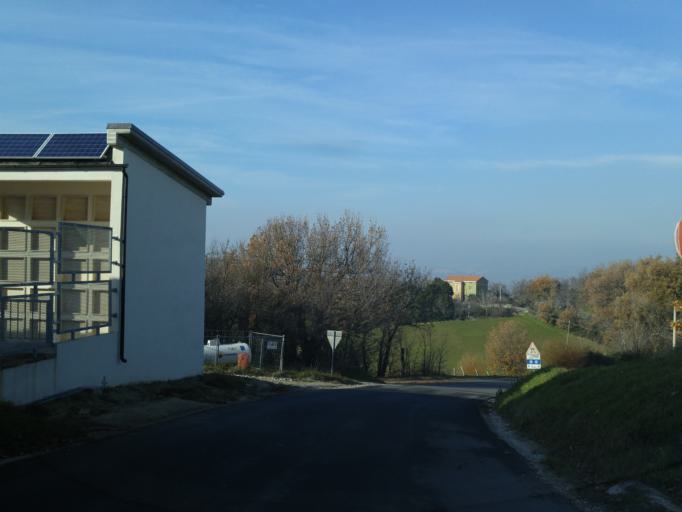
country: IT
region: The Marches
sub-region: Provincia di Pesaro e Urbino
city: Villanova
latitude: 43.7108
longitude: 12.9165
